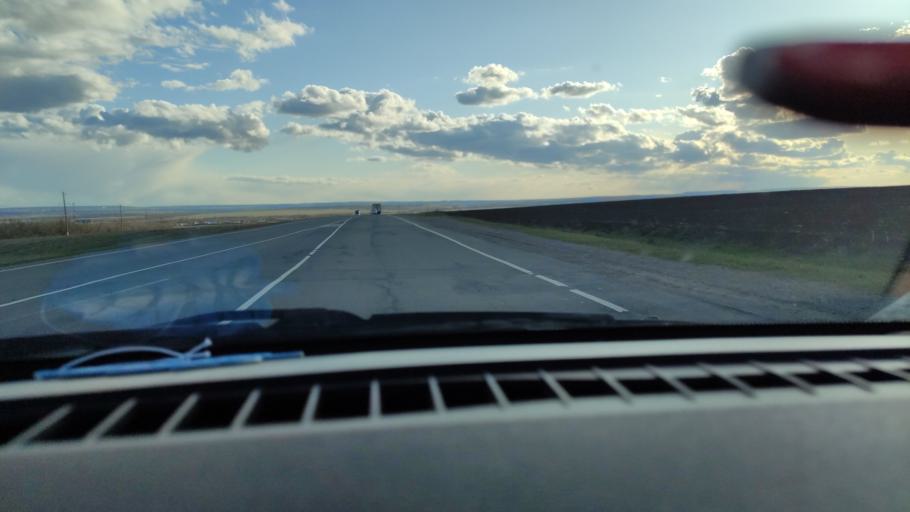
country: RU
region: Saratov
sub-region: Saratovskiy Rayon
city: Saratov
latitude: 51.7427
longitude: 46.0477
